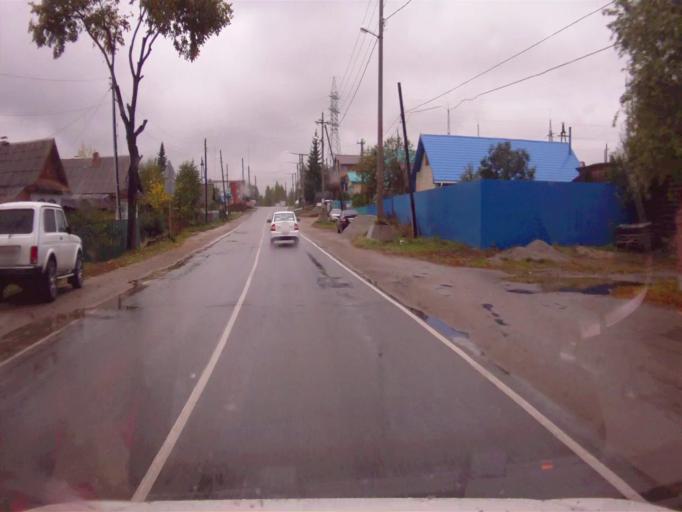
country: RU
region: Chelyabinsk
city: Kyshtym
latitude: 55.7250
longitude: 60.5234
